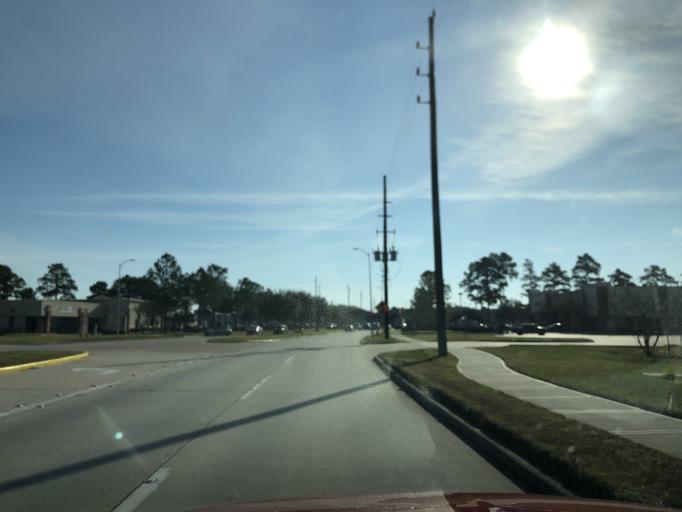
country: US
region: Texas
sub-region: Harris County
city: Tomball
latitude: 30.0340
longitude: -95.5572
